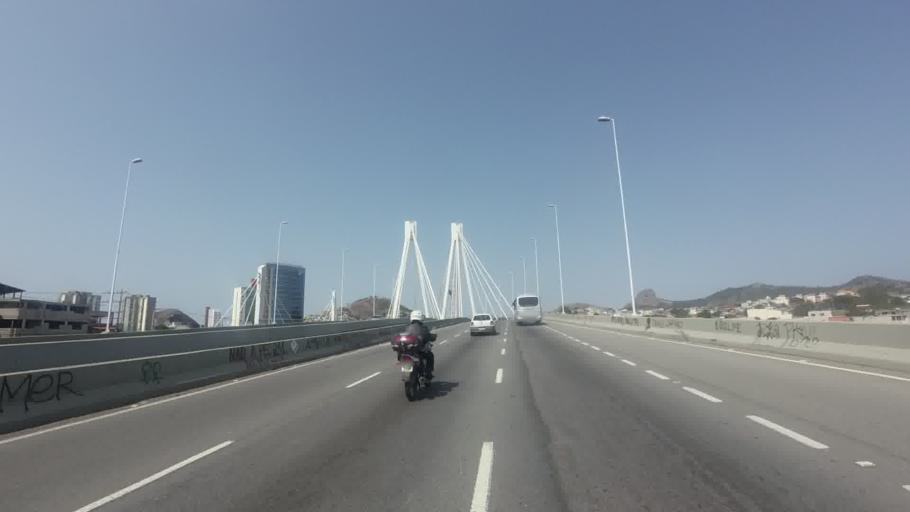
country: BR
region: Espirito Santo
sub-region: Vila Velha
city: Vila Velha
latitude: -20.2850
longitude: -40.3032
